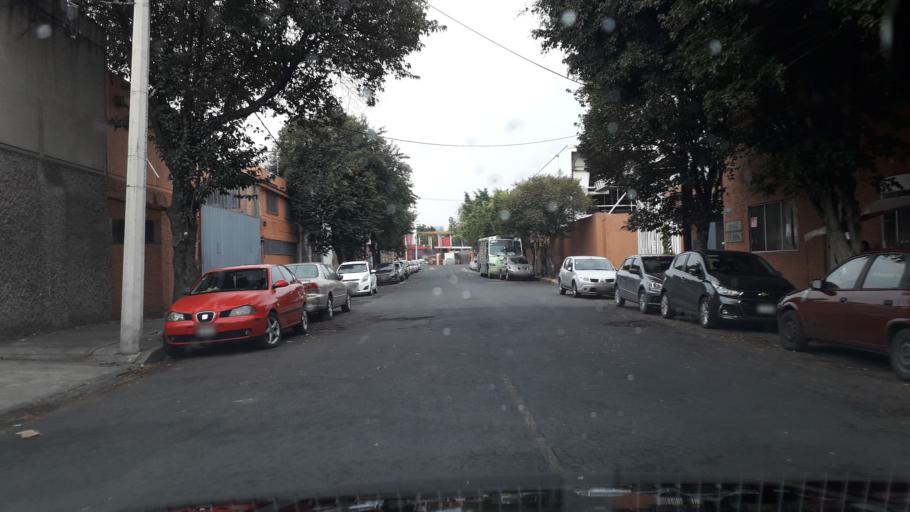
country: MX
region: Mexico City
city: Cuauhtemoc
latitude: 19.4571
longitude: -99.1594
